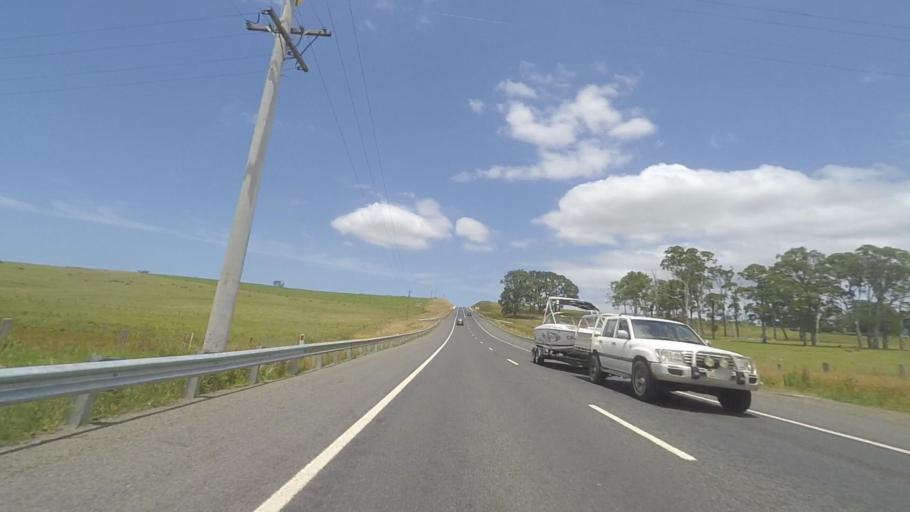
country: AU
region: New South Wales
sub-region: Shoalhaven Shire
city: Milton
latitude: -35.2826
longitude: 150.4222
